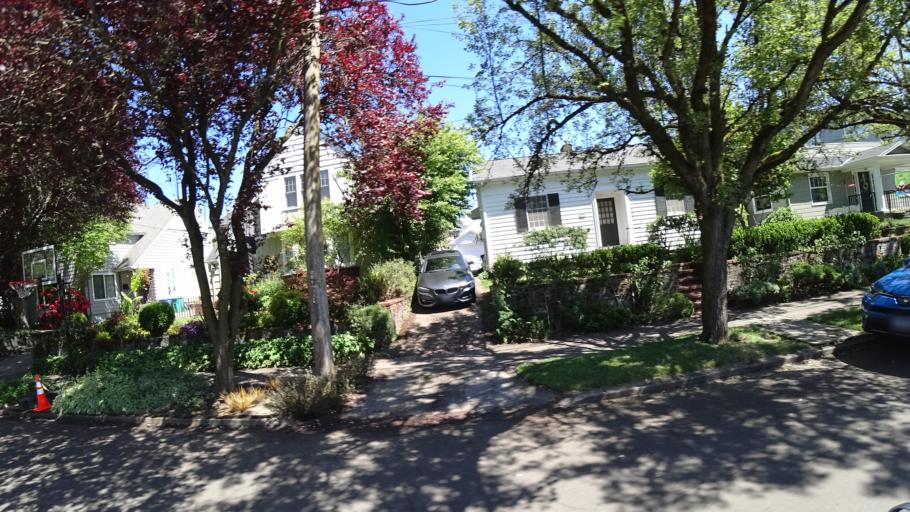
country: US
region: Oregon
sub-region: Multnomah County
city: Portland
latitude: 45.5090
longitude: -122.6413
